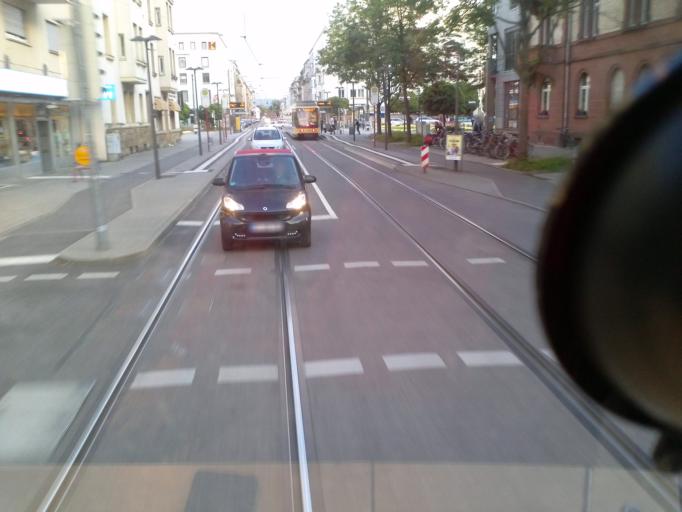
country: DE
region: Baden-Wuerttemberg
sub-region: Karlsruhe Region
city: Karlsruhe
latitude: 48.9982
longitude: 8.3937
